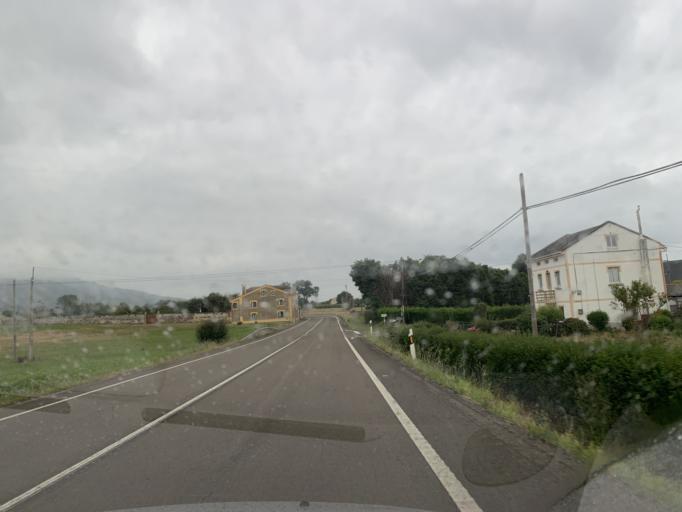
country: ES
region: Galicia
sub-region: Provincia de Lugo
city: Ribadeo
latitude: 43.5470
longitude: -7.1157
